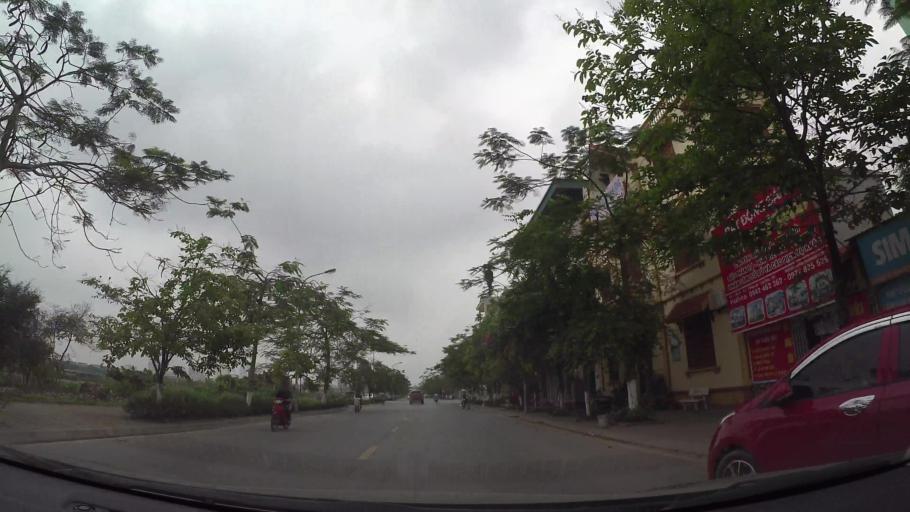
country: VN
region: Ha Noi
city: Trau Quy
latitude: 21.0504
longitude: 105.9217
